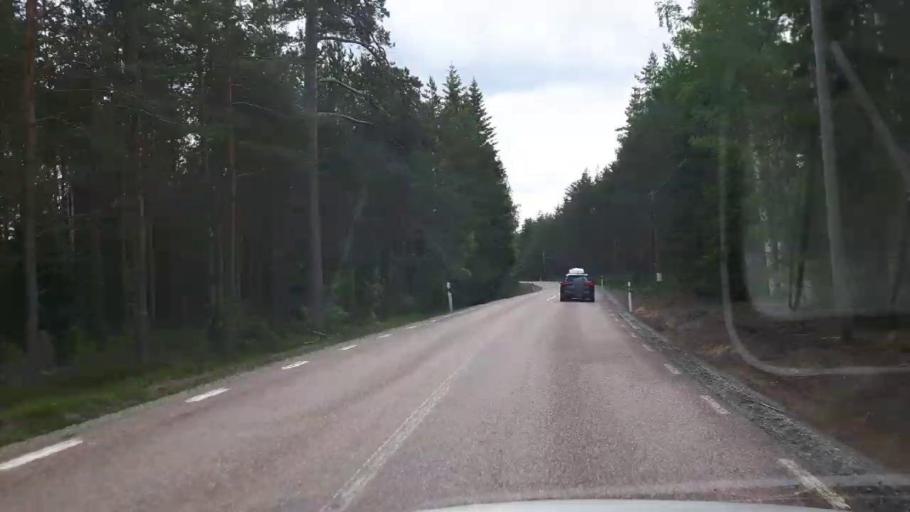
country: SE
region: Vaestmanland
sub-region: Skinnskattebergs Kommun
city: Skinnskatteberg
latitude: 59.8148
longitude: 15.8398
